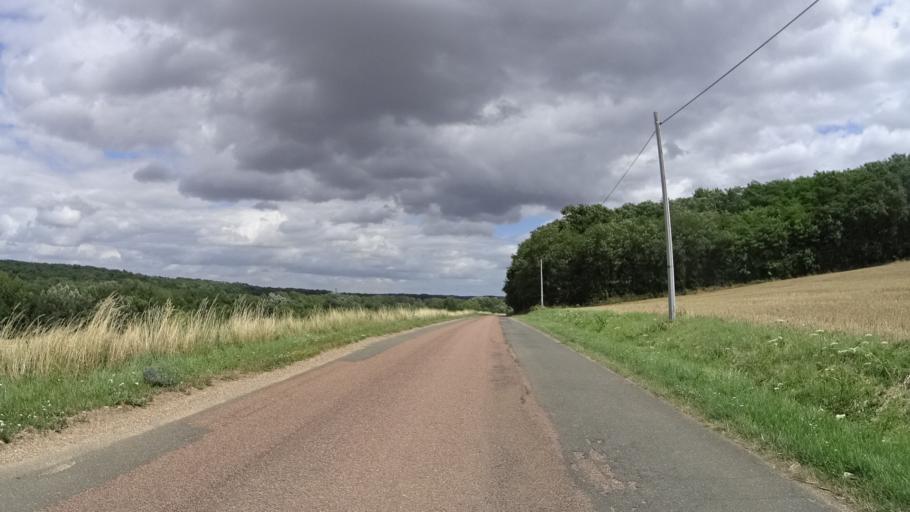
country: FR
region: Centre
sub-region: Departement du Loiret
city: Douchy
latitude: 47.9370
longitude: 3.0214
